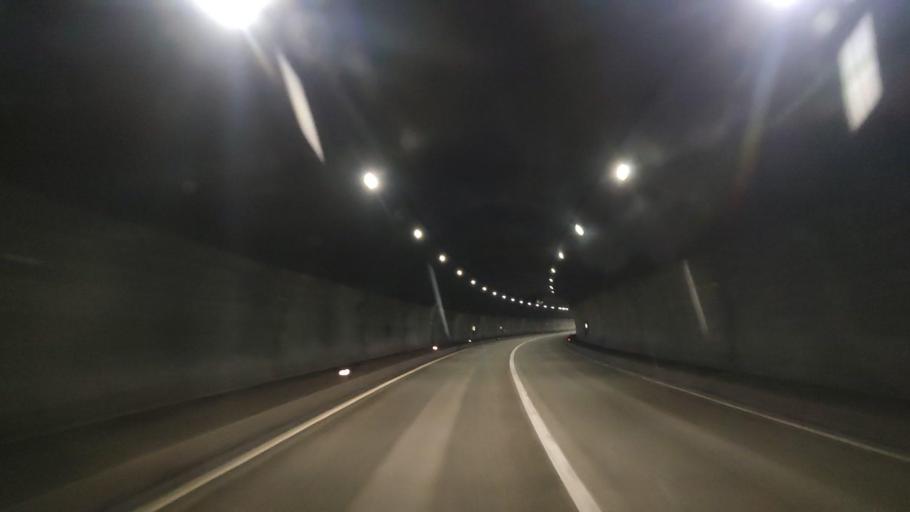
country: JP
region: Nagano
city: Omachi
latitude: 36.5459
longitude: 137.8455
